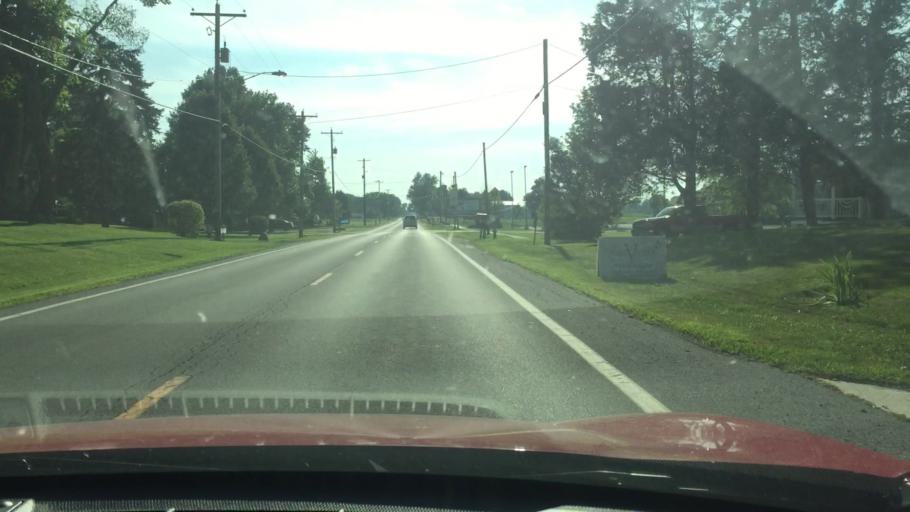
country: US
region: Ohio
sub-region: Hardin County
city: Ada
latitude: 40.7767
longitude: -83.8305
